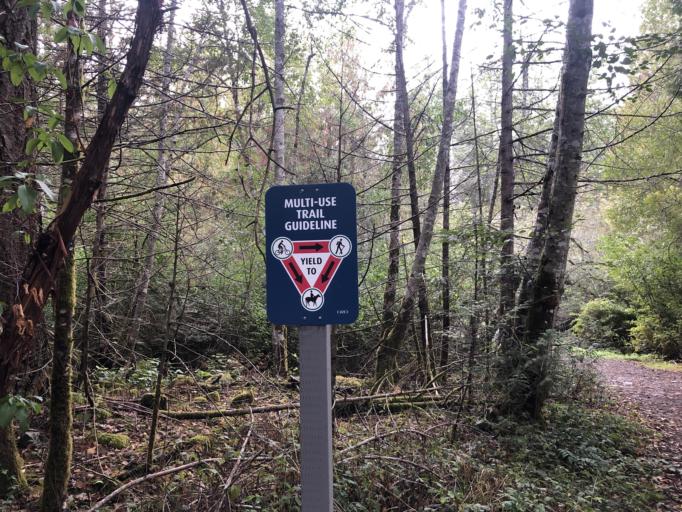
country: CA
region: British Columbia
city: Langford
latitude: 48.4716
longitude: -123.4890
